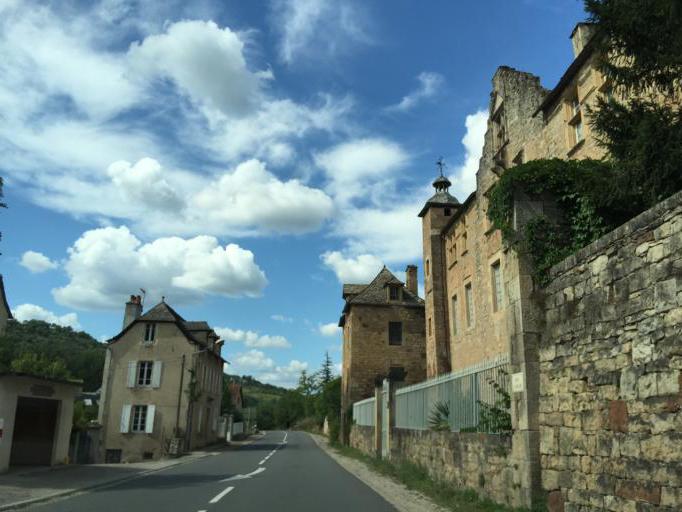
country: FR
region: Midi-Pyrenees
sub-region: Departement de l'Aveyron
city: Marcillac-Vallon
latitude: 44.4528
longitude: 2.4737
